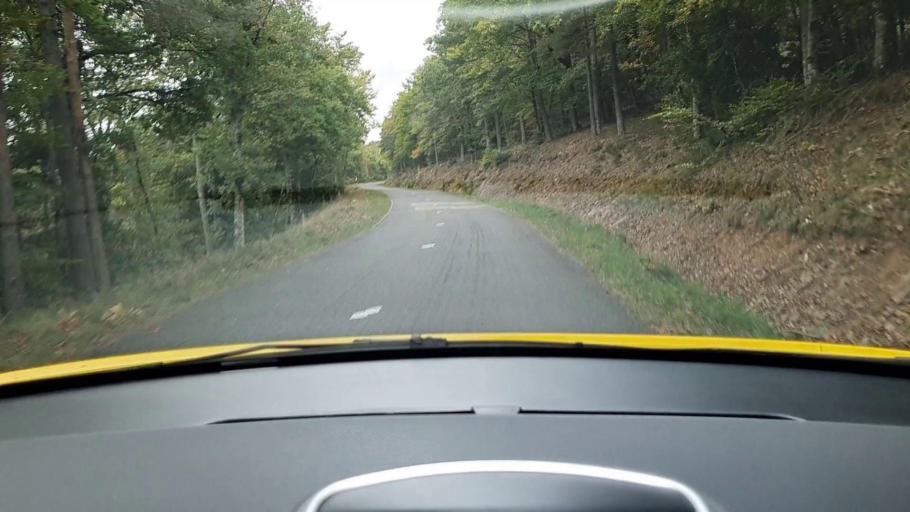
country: FR
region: Languedoc-Roussillon
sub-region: Departement de la Lozere
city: Meyrueis
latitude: 44.0811
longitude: 3.4150
